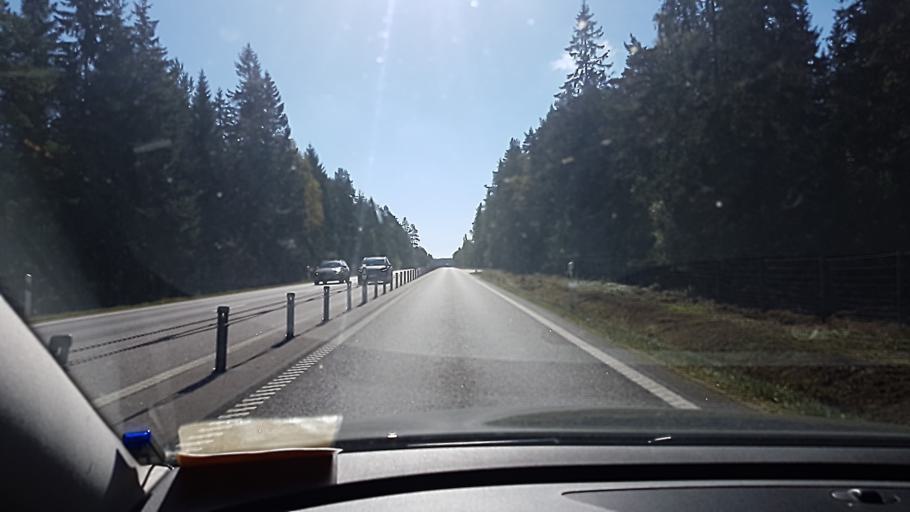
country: SE
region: Kronoberg
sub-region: Lessebo Kommun
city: Hovmantorp
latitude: 56.8240
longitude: 15.0883
